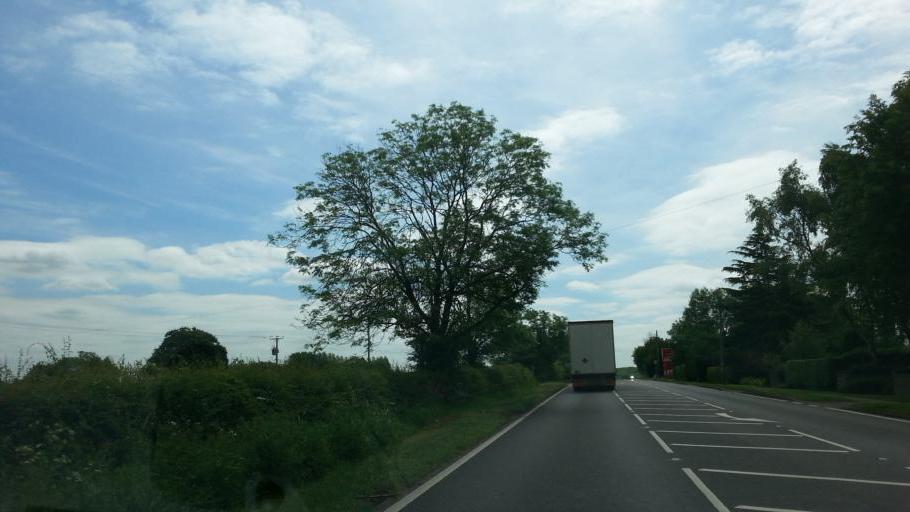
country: GB
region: England
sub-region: Nottinghamshire
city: Cotgrave
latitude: 52.8703
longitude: -1.0484
